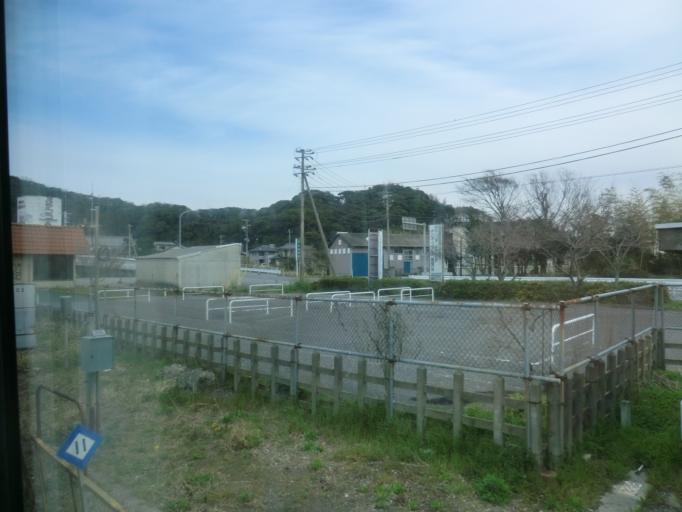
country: JP
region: Chiba
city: Kimitsu
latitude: 35.2610
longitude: 139.8759
